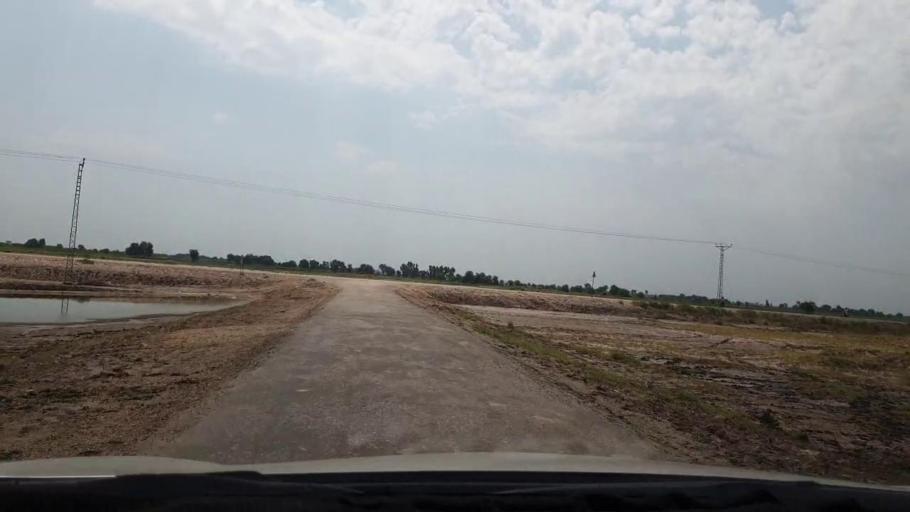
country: PK
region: Sindh
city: Ratodero
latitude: 27.8349
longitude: 68.3047
